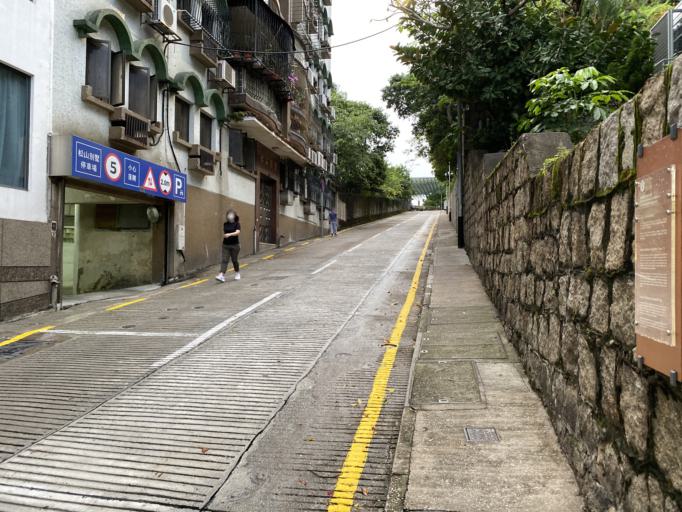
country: MO
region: Macau
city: Macau
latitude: 22.1959
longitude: 113.5487
